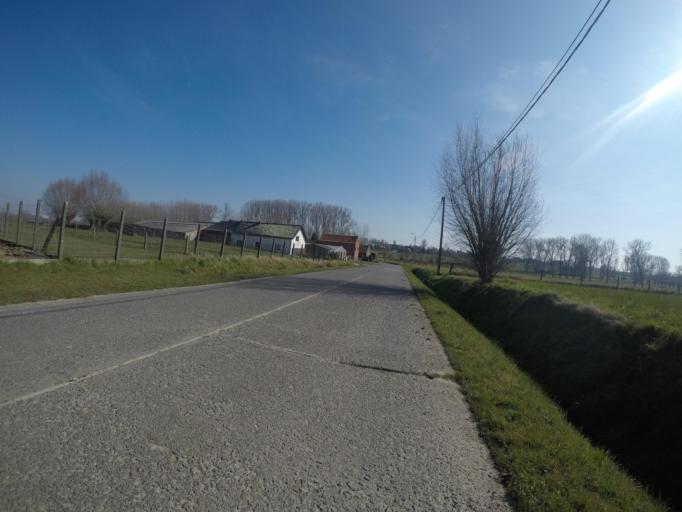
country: BE
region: Flanders
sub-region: Provincie Oost-Vlaanderen
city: Sint-Maria-Lierde
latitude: 50.7884
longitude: 3.8252
